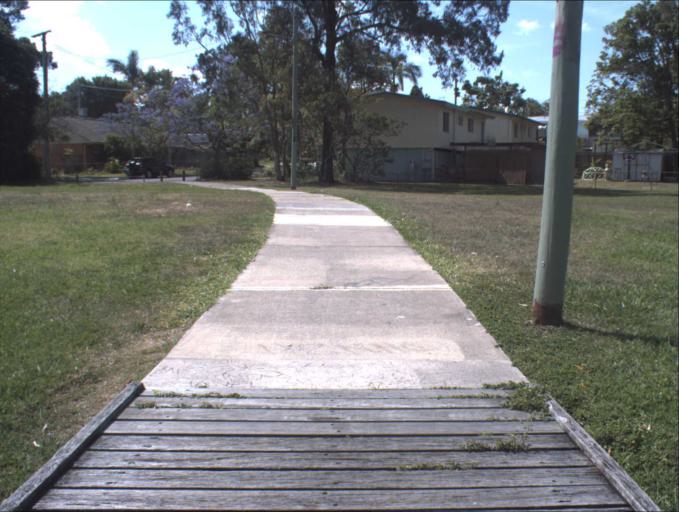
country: AU
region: Queensland
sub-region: Logan
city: Logan City
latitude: -27.6345
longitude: 153.1059
